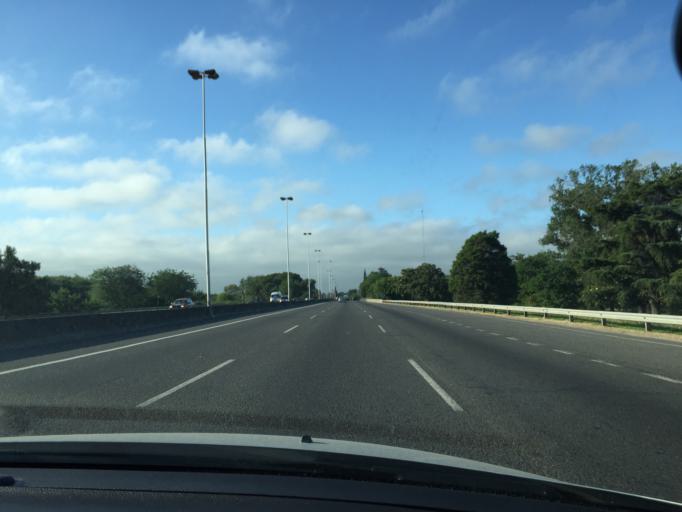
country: AR
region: Buenos Aires
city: San Justo
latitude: -34.7456
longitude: -58.5217
